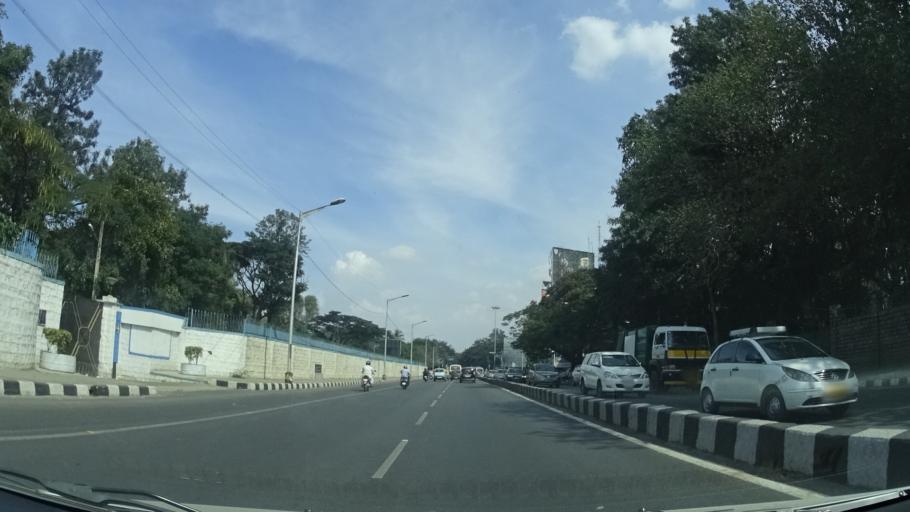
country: IN
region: Karnataka
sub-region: Bangalore Urban
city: Bangalore
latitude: 13.0148
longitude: 77.5820
